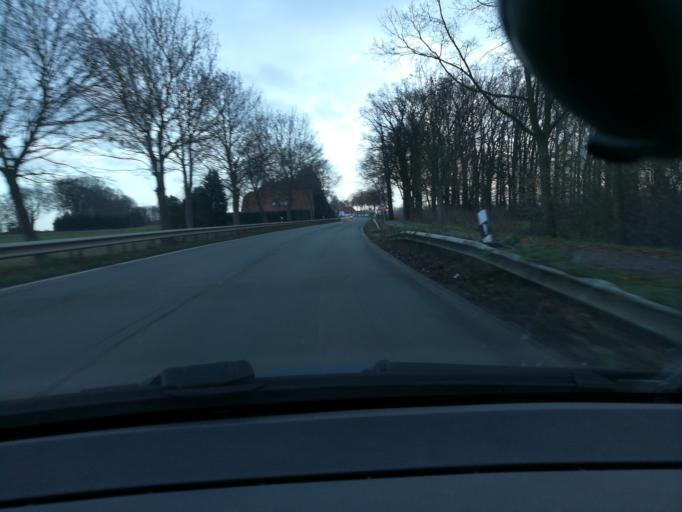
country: DE
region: North Rhine-Westphalia
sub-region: Regierungsbezirk Detmold
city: Hille
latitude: 52.3286
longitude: 8.7705
